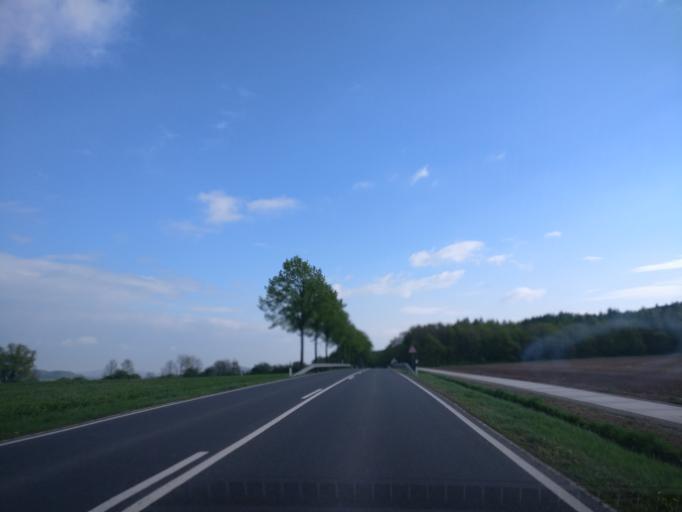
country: DE
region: Lower Saxony
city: Dransfeld
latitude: 51.4890
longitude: 9.7277
